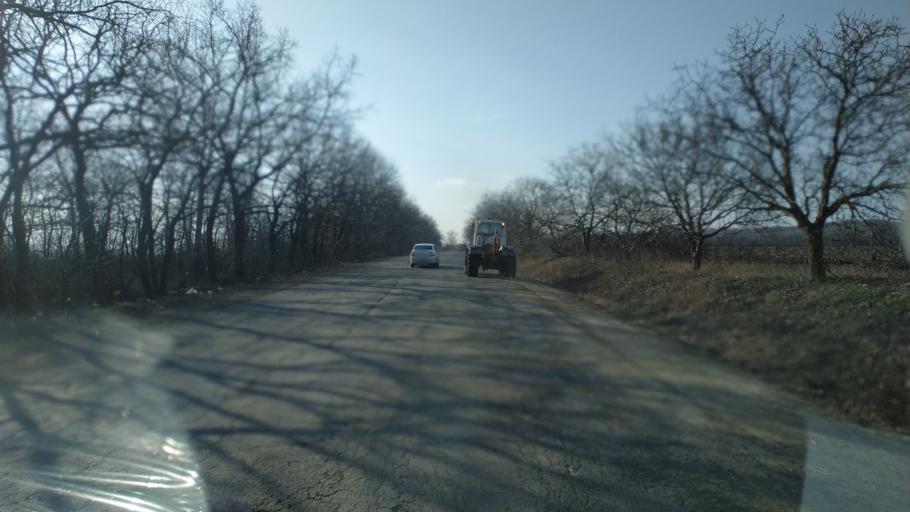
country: MD
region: Chisinau
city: Singera
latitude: 46.8708
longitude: 29.0398
